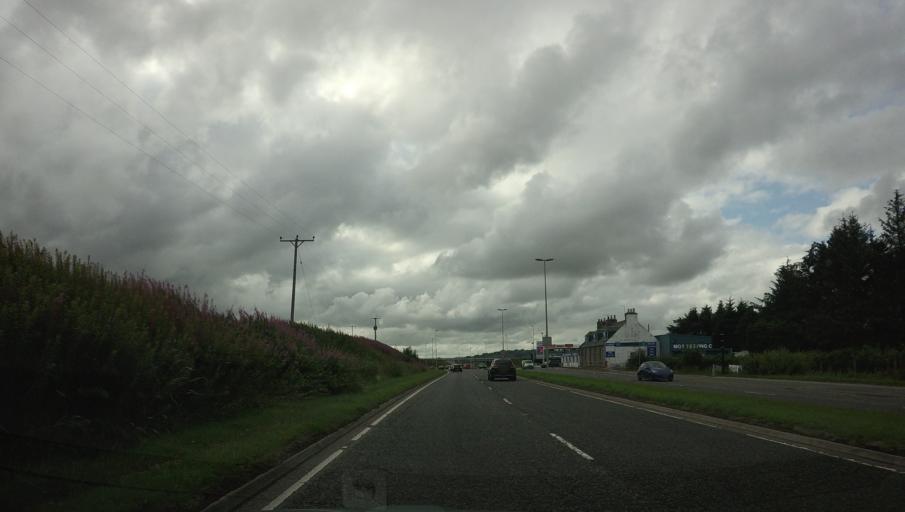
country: GB
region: Scotland
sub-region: Aberdeenshire
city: Westhill
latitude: 57.1465
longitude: -2.2363
